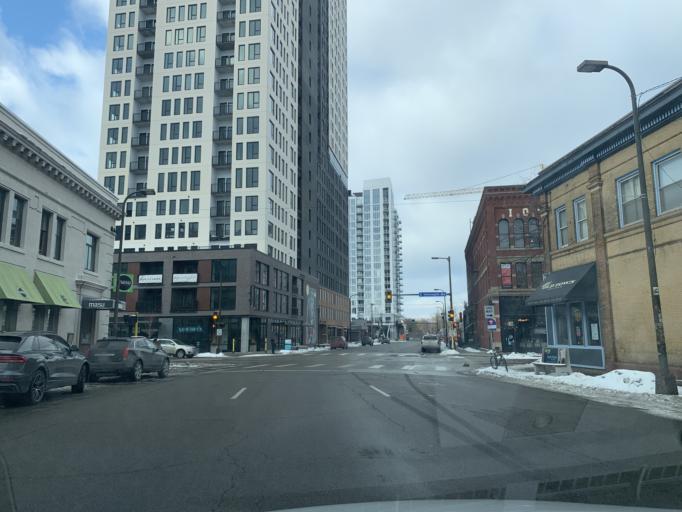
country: US
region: Minnesota
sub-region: Hennepin County
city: Minneapolis
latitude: 44.9882
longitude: -93.2546
